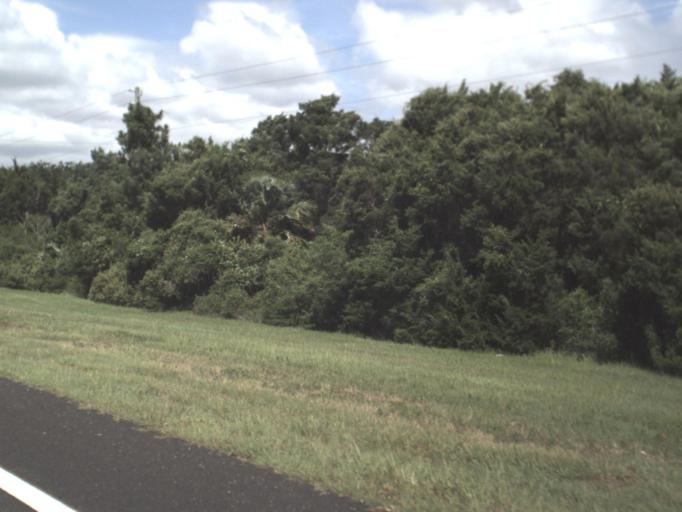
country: US
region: Florida
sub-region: Nassau County
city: Fernandina Beach
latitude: 30.6245
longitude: -81.4916
